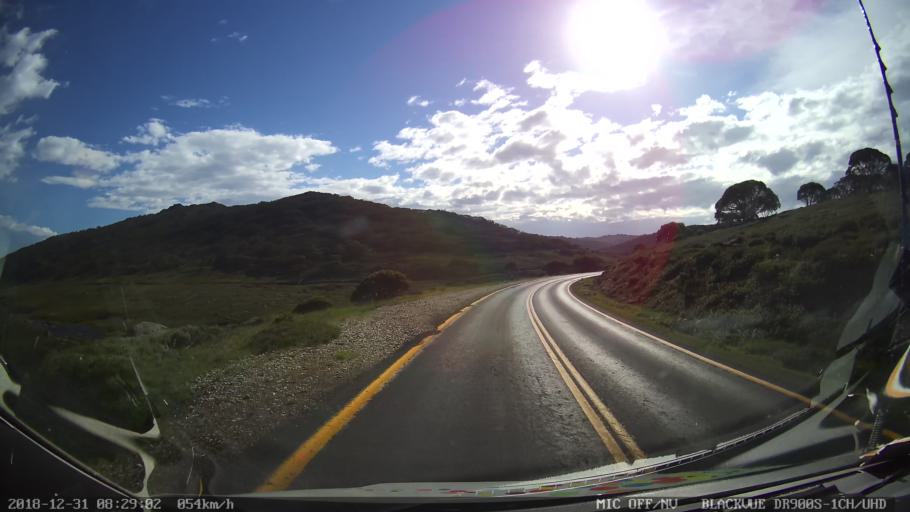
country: AU
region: New South Wales
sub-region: Snowy River
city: Jindabyne
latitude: -36.4265
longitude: 148.3511
